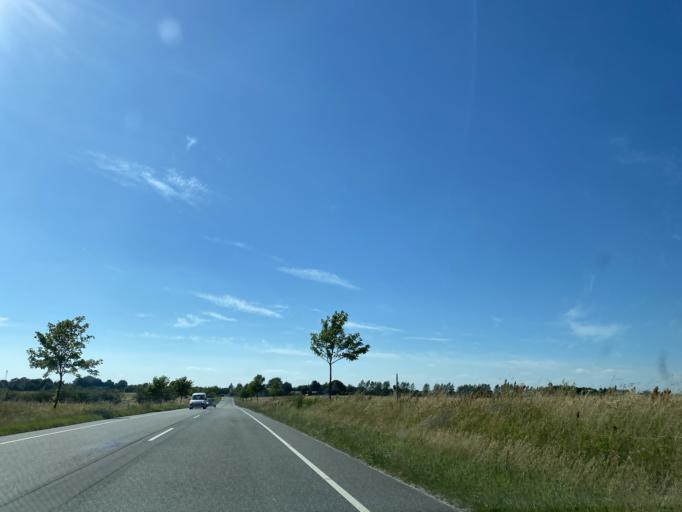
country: DK
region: Central Jutland
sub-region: Hedensted Kommune
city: Torring
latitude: 55.8672
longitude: 9.3751
